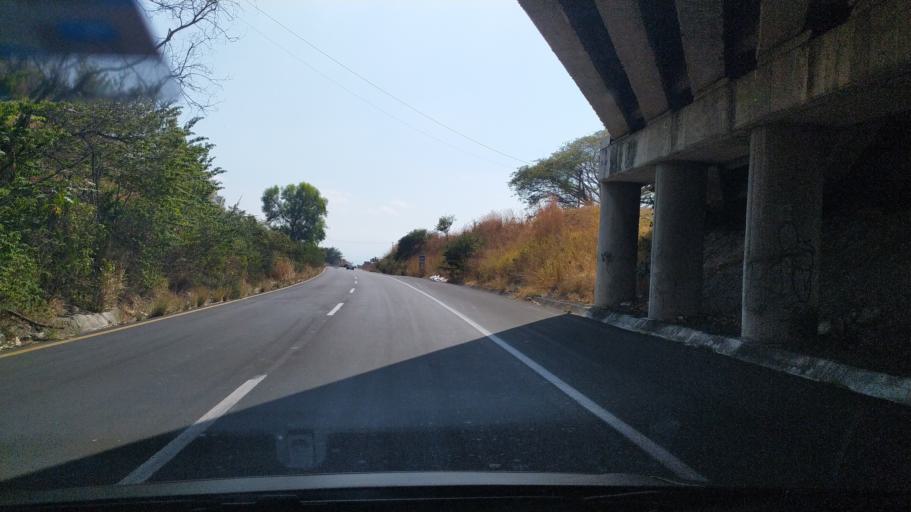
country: MX
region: Colima
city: Colima
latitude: 19.2640
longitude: -103.6819
